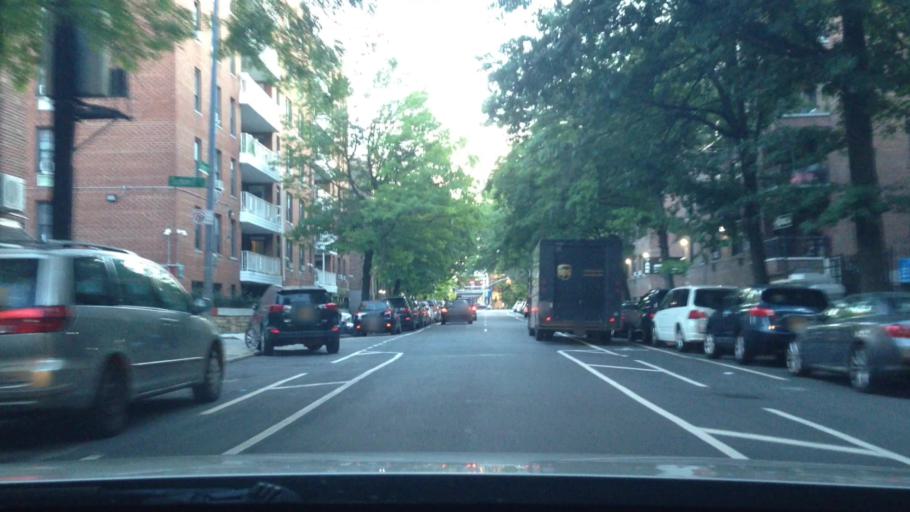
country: US
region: New York
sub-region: Queens County
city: Jamaica
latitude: 40.7556
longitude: -73.8311
